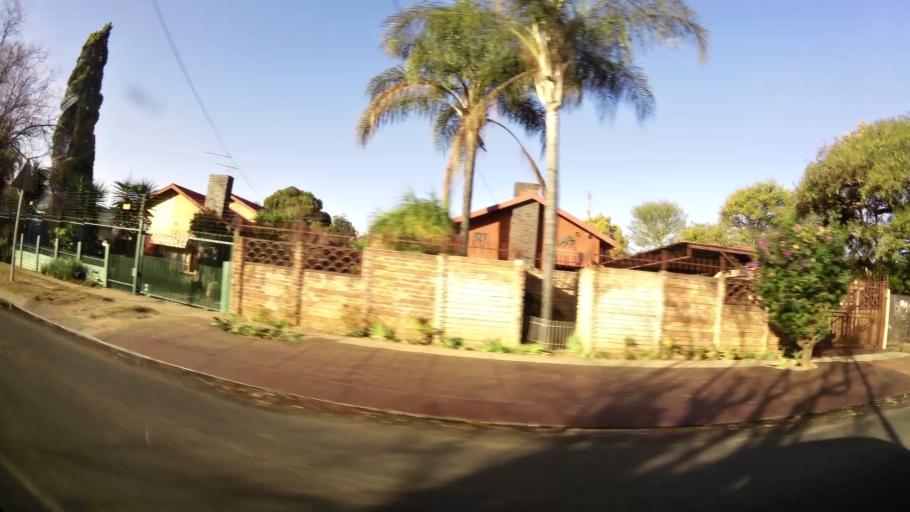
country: ZA
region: Gauteng
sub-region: City of Tshwane Metropolitan Municipality
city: Pretoria
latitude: -25.7108
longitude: 28.2059
